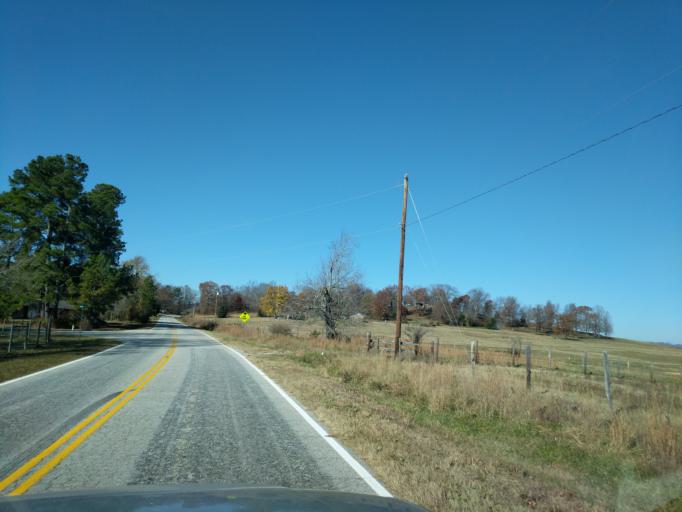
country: US
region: South Carolina
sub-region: Spartanburg County
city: Landrum
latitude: 35.0912
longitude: -82.2209
